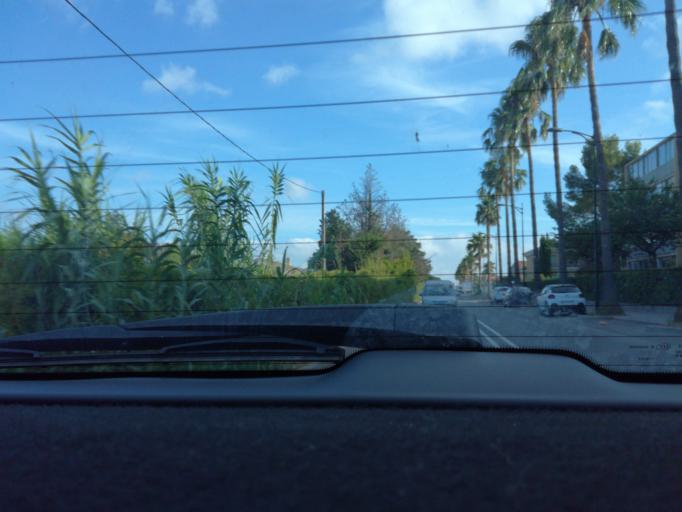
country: FR
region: Provence-Alpes-Cote d'Azur
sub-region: Departement du Var
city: Hyeres
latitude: 43.1103
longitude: 6.1301
